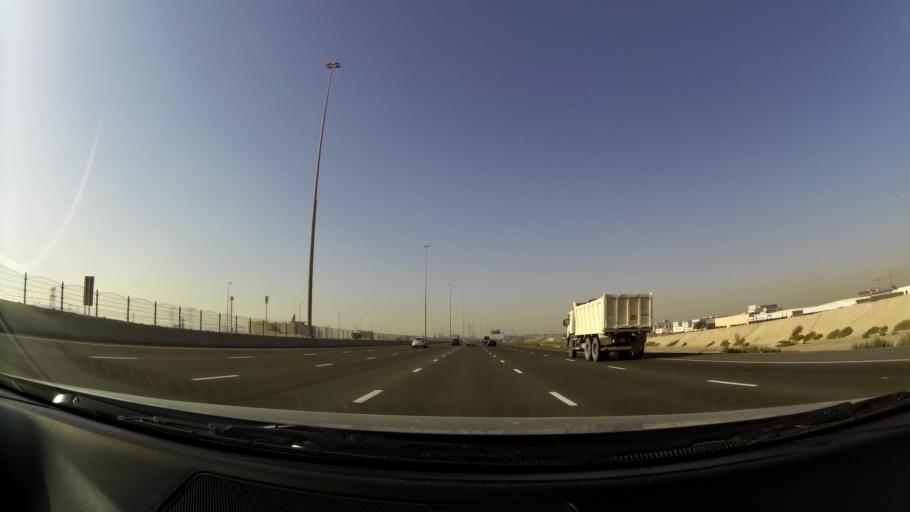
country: AE
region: Dubai
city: Dubai
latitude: 25.0002
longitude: 55.1486
